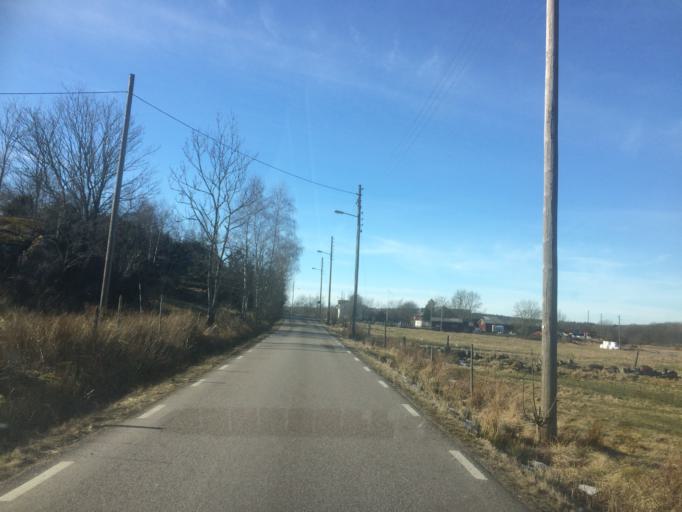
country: SE
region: Vaestra Goetaland
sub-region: Goteborg
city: Torslanda
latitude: 57.7900
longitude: 11.8586
